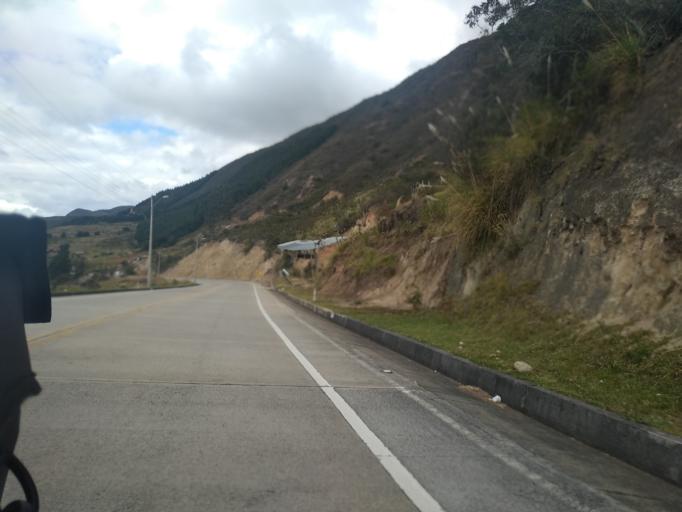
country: EC
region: Azuay
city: Cuenca
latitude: -3.3929
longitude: -79.1808
